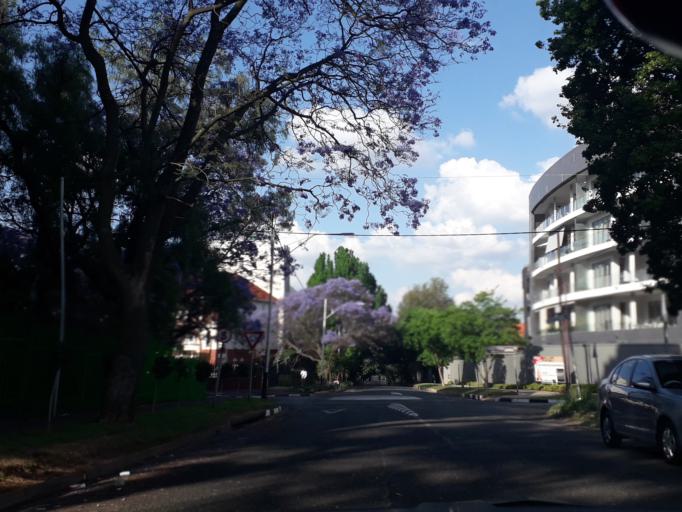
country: ZA
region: Gauteng
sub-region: City of Johannesburg Metropolitan Municipality
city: Johannesburg
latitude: -26.1479
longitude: 28.0457
